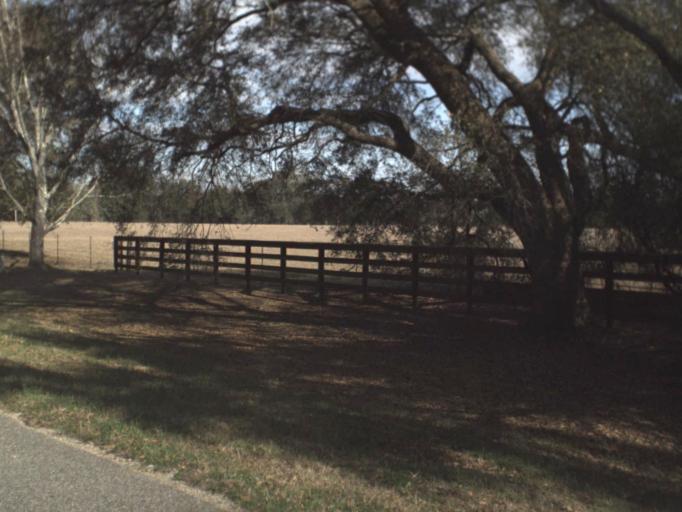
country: US
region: Florida
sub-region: Jackson County
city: Malone
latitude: 30.9870
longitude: -85.1872
